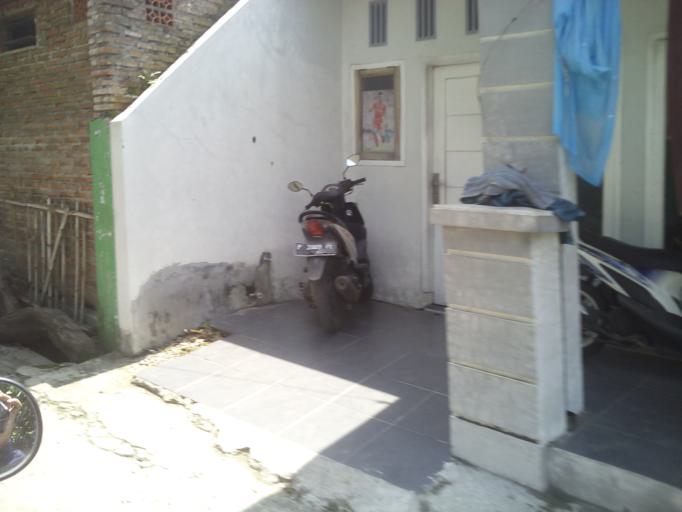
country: ID
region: East Java
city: Sumbersari Wetan
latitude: -8.1797
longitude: 113.7174
